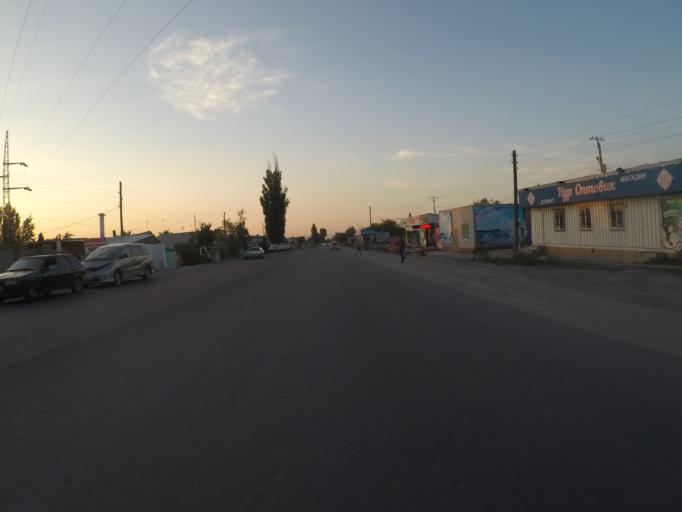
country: KG
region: Chuy
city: Lebedinovka
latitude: 42.8041
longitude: 74.6482
